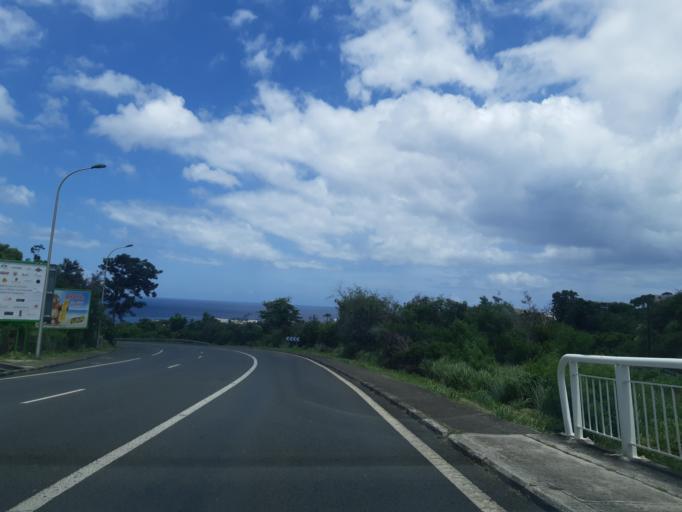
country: GP
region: Guadeloupe
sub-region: Guadeloupe
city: Basse-Terre
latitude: 15.9994
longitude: -61.7251
